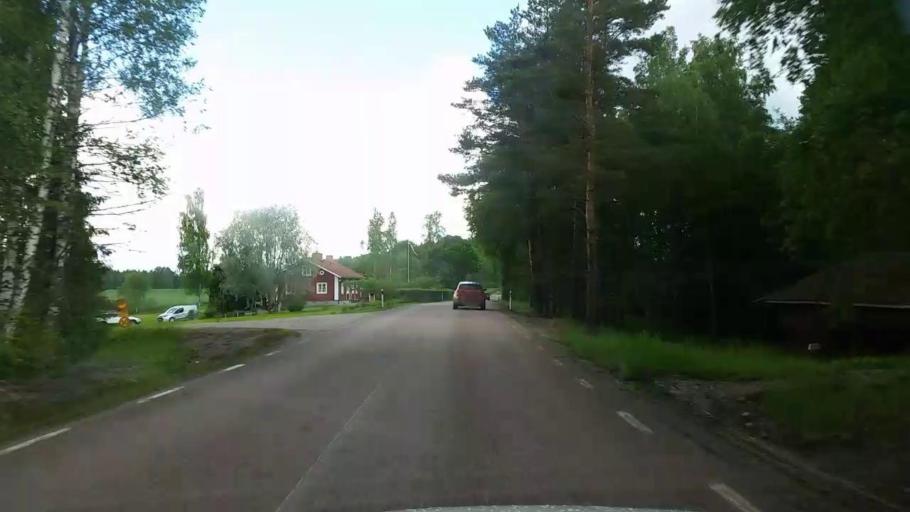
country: SE
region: Vaestmanland
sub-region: Skinnskattebergs Kommun
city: Skinnskatteberg
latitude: 59.8478
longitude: 15.8418
